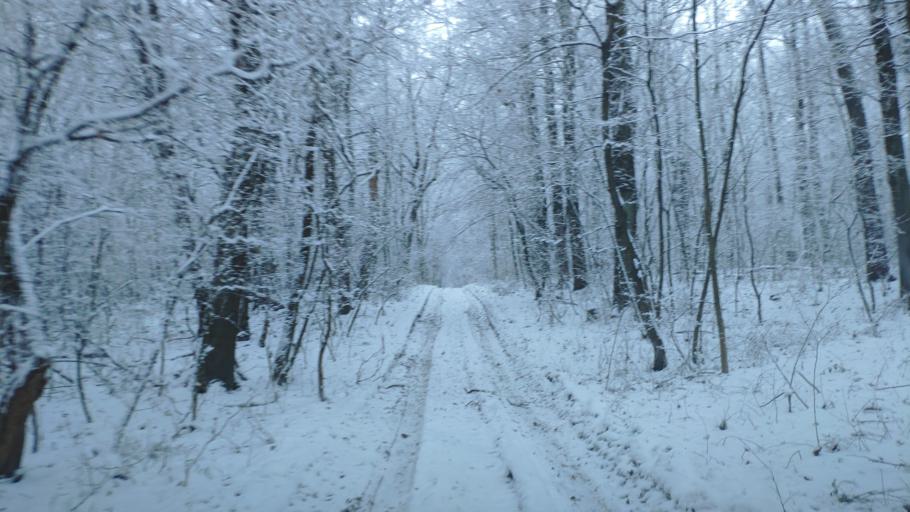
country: SK
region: Kosicky
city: Kosice
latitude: 48.6442
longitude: 21.1876
